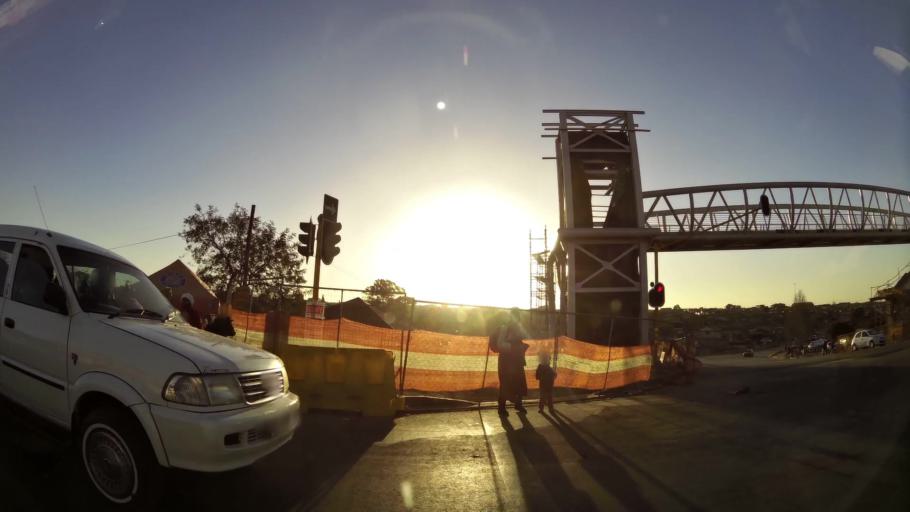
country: ZA
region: Gauteng
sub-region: Ekurhuleni Metropolitan Municipality
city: Tembisa
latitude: -26.0205
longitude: 28.1996
